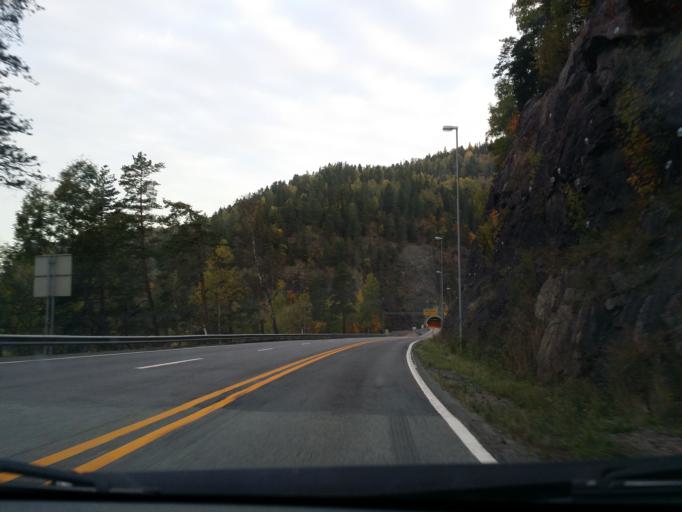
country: NO
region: Buskerud
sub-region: Hole
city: Vik
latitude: 59.9896
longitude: 10.3023
